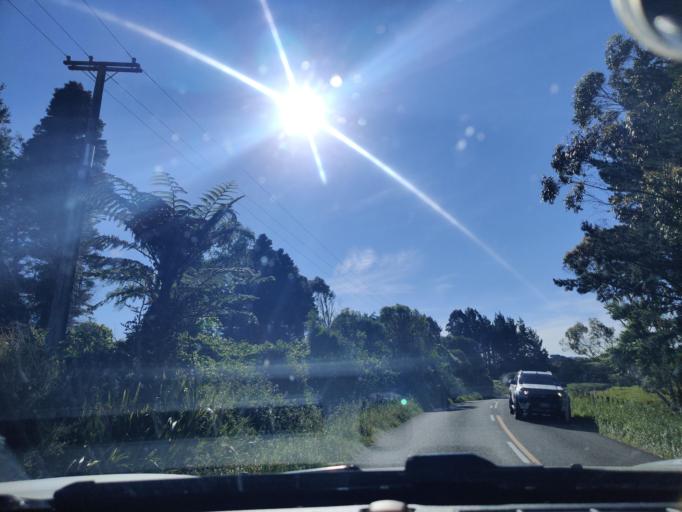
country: NZ
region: Manawatu-Wanganui
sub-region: Palmerston North City
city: Palmerston North
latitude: -40.5151
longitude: 175.7445
